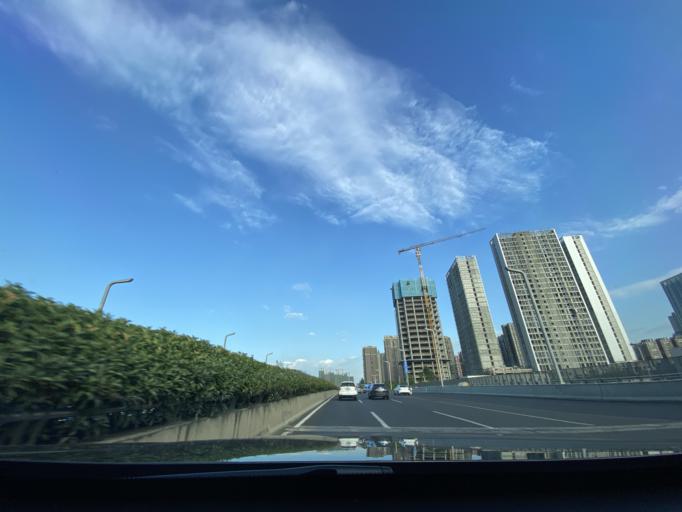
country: CN
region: Sichuan
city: Chengdu
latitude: 30.6387
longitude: 104.1414
